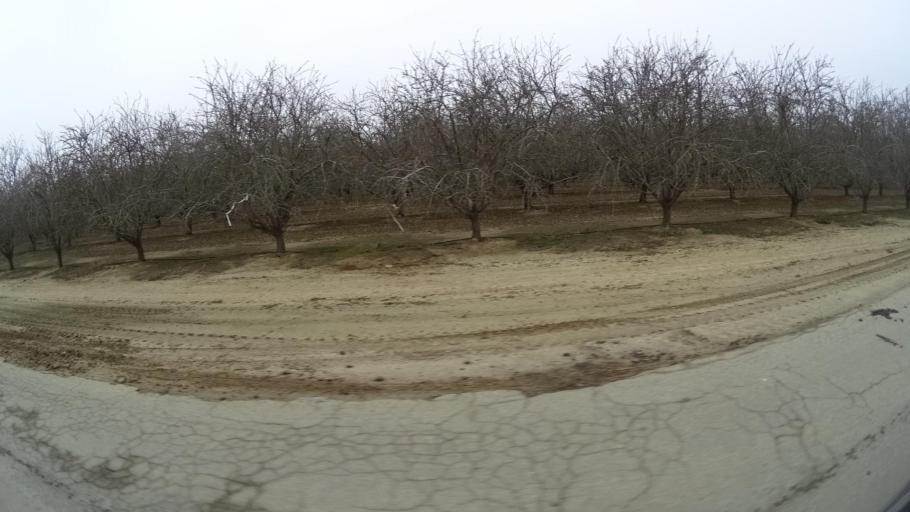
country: US
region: California
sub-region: Kern County
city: Wasco
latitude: 35.5630
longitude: -119.4919
